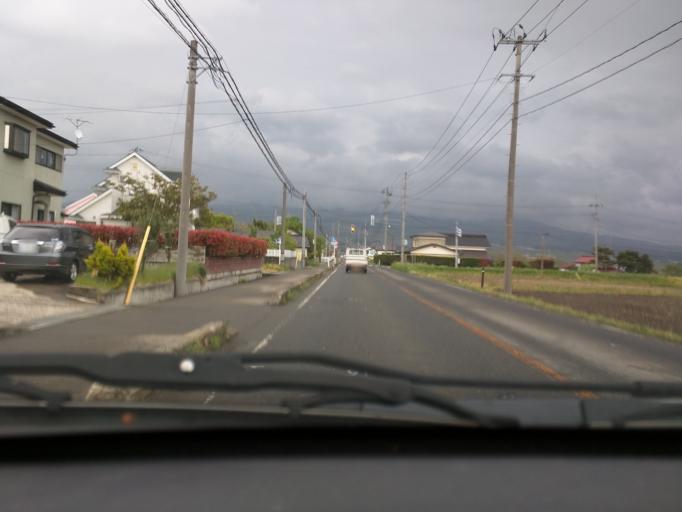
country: JP
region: Fukushima
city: Kitakata
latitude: 37.6470
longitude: 139.8998
